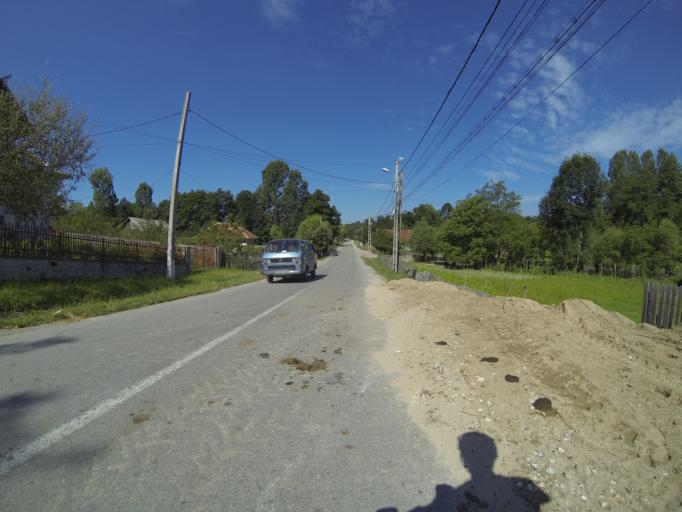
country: RO
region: Gorj
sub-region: Comuna Polovragi
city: Polovragi
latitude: 45.1690
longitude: 23.8384
